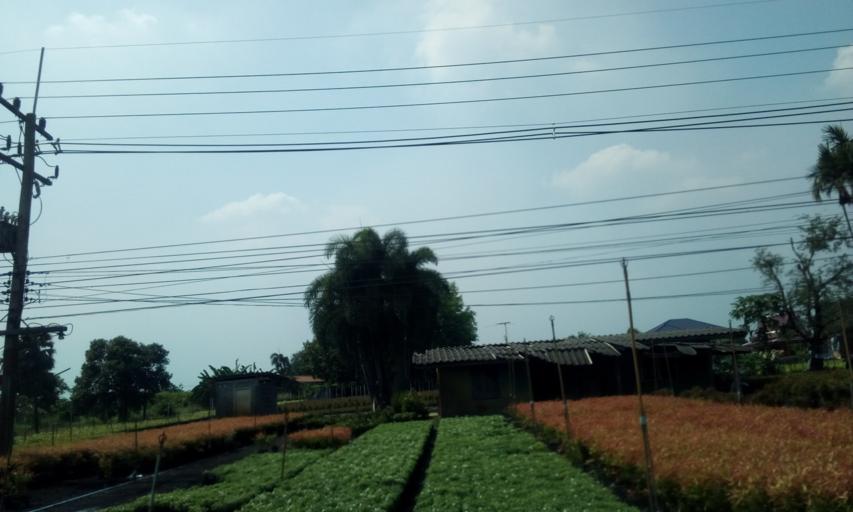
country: TH
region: Nakhon Nayok
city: Ongkharak
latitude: 14.1189
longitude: 100.9431
